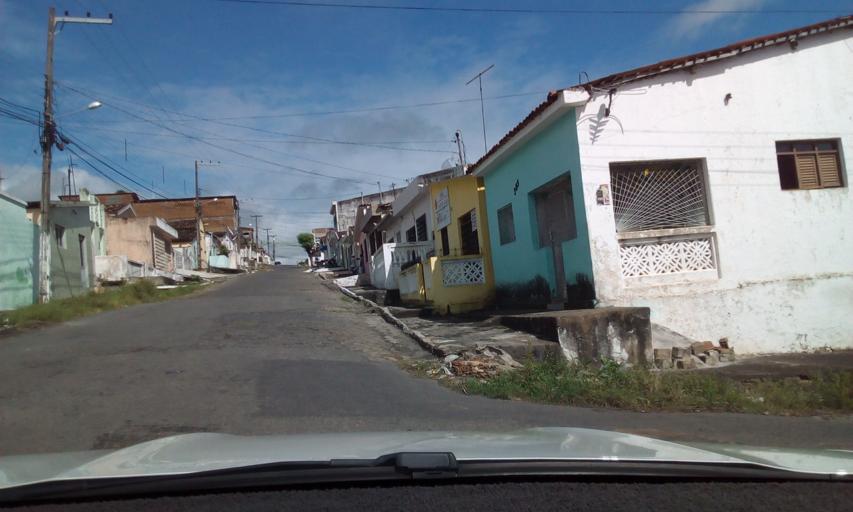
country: BR
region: Paraiba
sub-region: Santa Rita
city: Santa Rita
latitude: -7.1275
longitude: -34.9778
